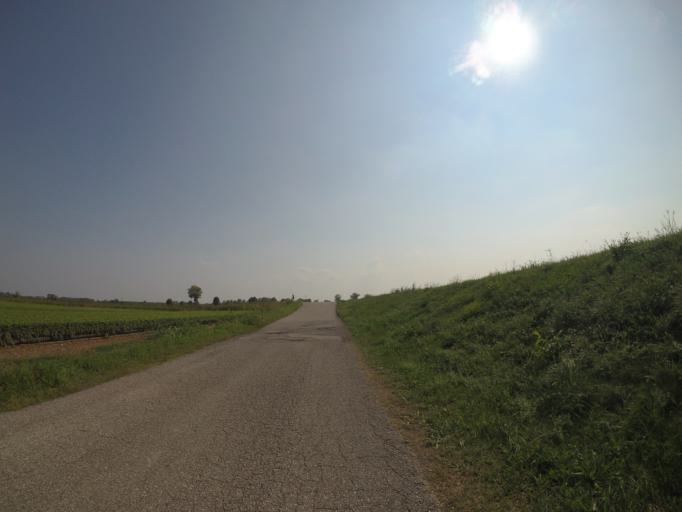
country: IT
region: Friuli Venezia Giulia
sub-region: Provincia di Udine
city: Camino al Tagliamento
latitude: 45.9261
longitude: 12.9237
